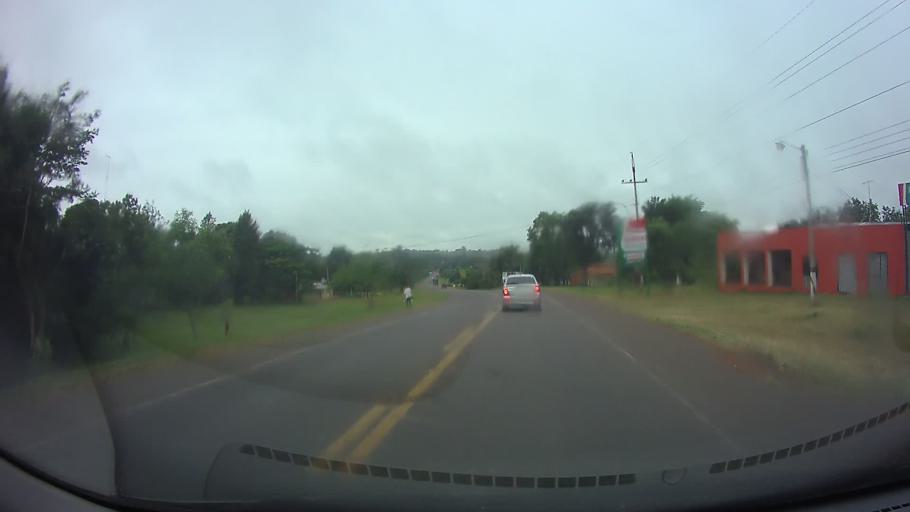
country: PY
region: Central
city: Ita
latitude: -25.5380
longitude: -57.3228
